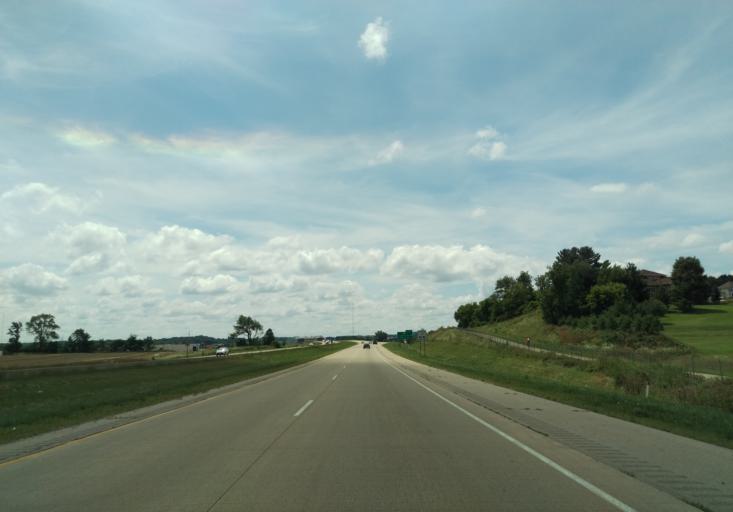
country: US
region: Wisconsin
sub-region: Dane County
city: Middleton
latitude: 43.1180
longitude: -89.5158
